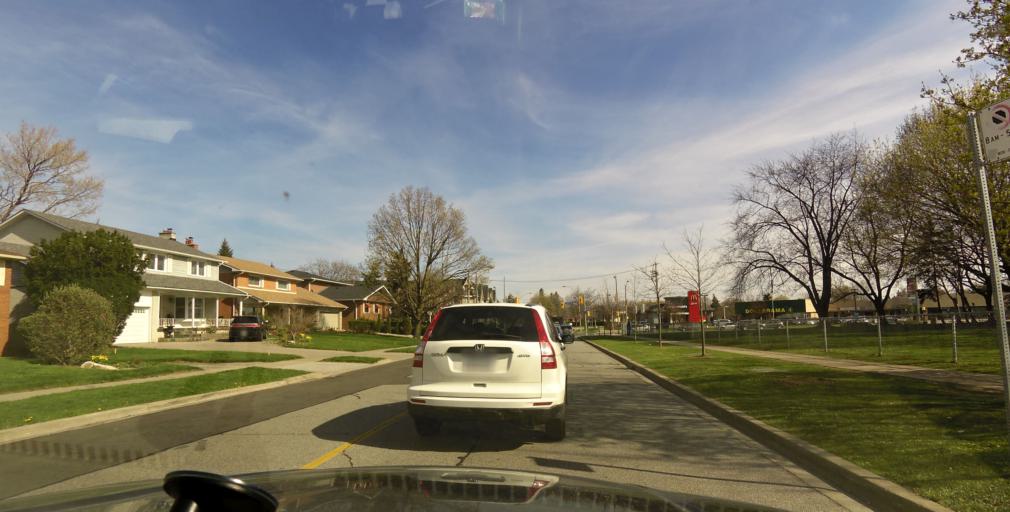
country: CA
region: Ontario
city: Etobicoke
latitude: 43.6327
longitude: -79.5758
